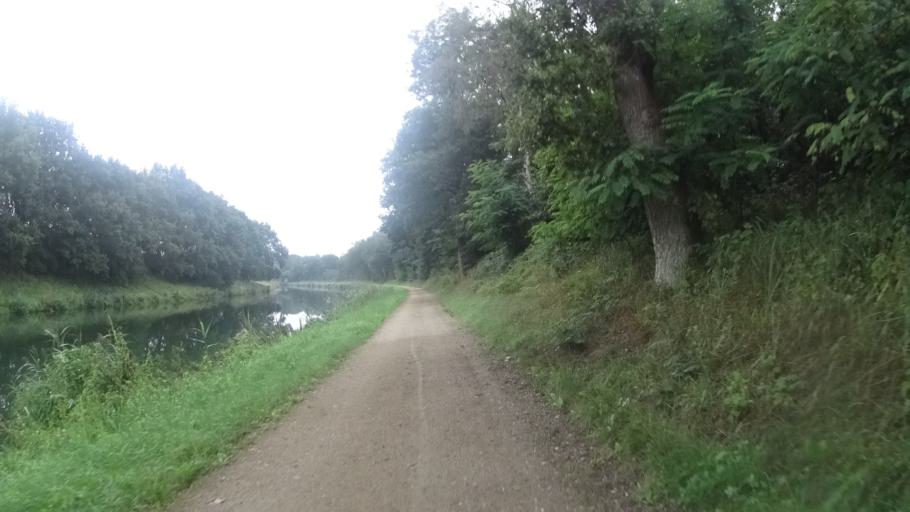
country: DE
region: Schleswig-Holstein
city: Grambek
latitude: 53.5858
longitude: 10.6665
